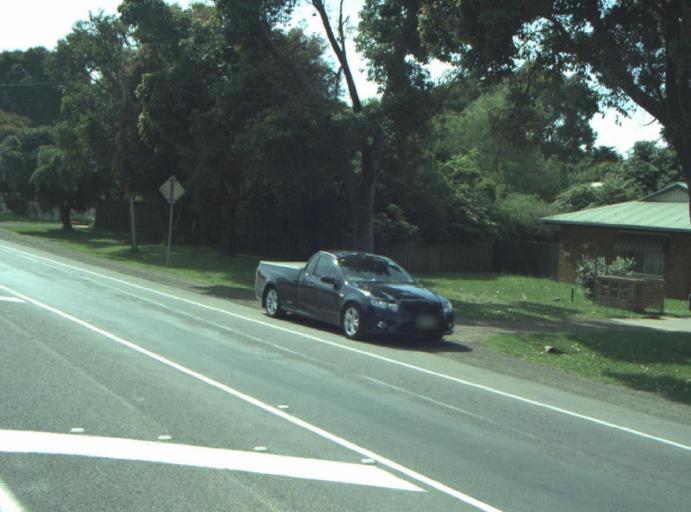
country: AU
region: Victoria
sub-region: Greater Geelong
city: Clifton Springs
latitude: -38.1788
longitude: 144.5606
